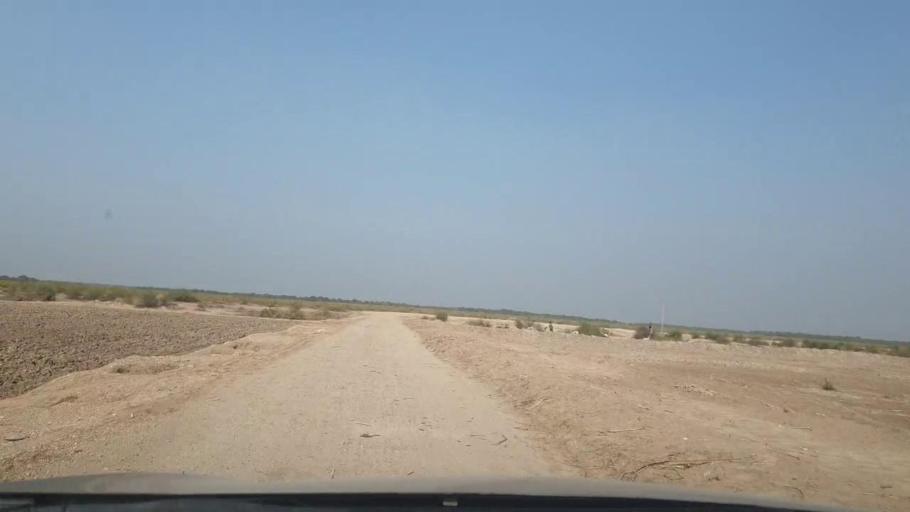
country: PK
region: Sindh
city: Tando Allahyar
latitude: 25.5693
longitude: 68.8256
